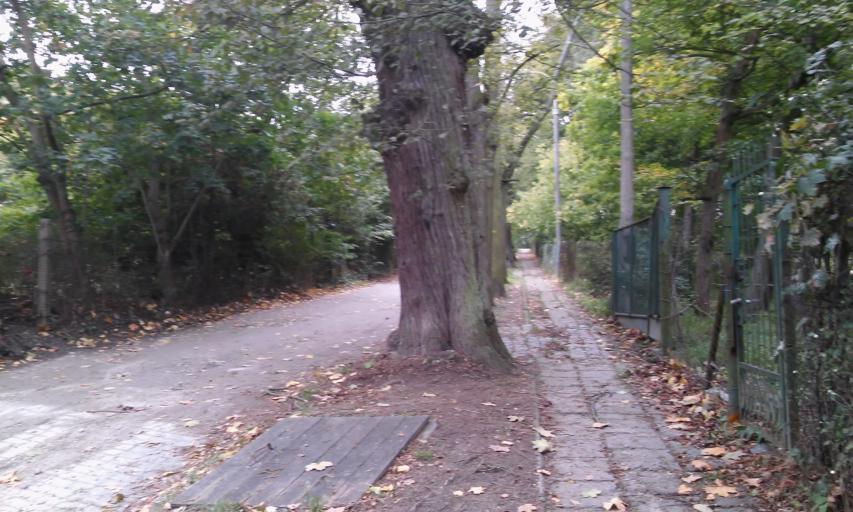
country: PL
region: Pomeranian Voivodeship
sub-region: Sopot
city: Sopot
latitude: 54.4054
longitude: 18.5597
